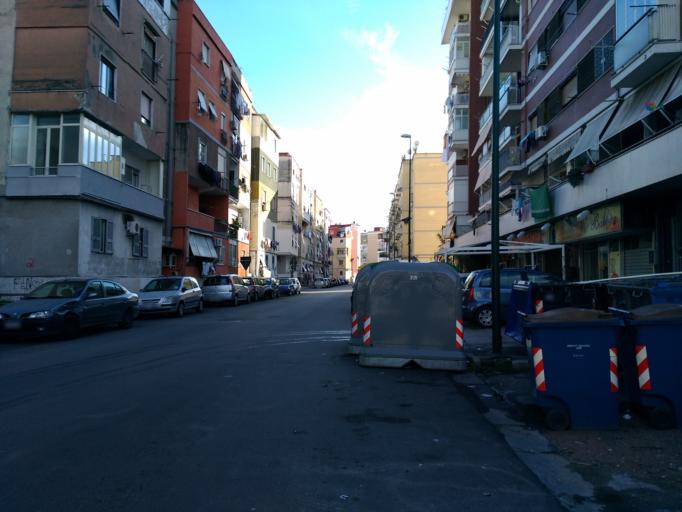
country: IT
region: Campania
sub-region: Provincia di Napoli
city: Arpino
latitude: 40.8596
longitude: 14.2928
